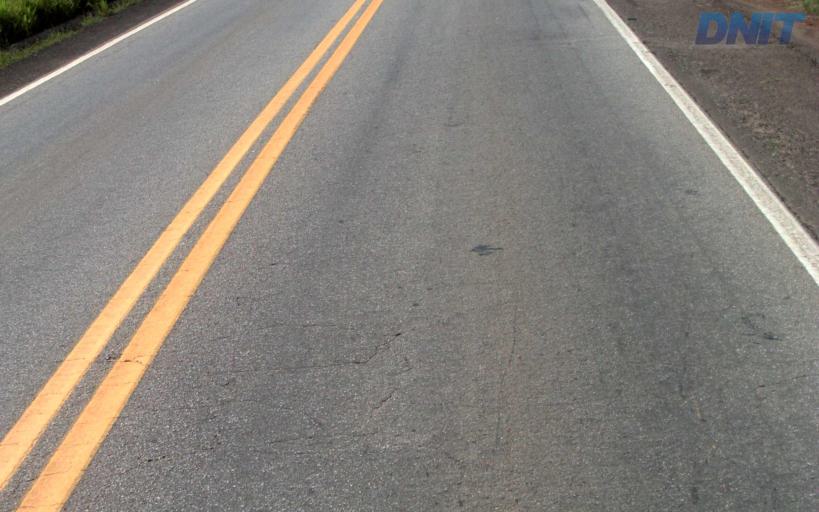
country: BR
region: Minas Gerais
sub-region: Ipaba
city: Ipaba
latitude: -19.4006
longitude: -42.4836
